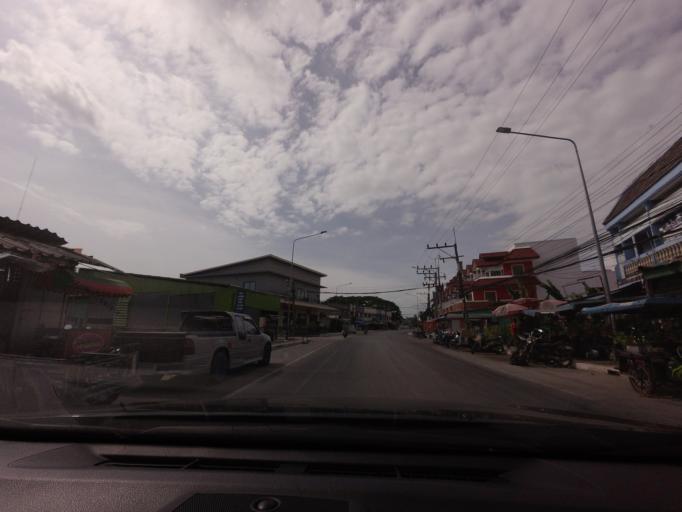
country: TH
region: Pattani
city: Pattani
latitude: 6.8766
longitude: 101.2480
